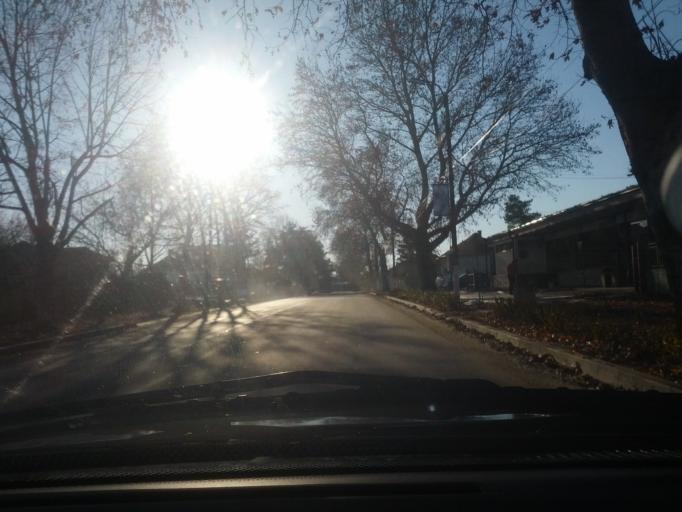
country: BG
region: Vratsa
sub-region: Obshtina Miziya
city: Miziya
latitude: 43.6884
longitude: 23.8062
